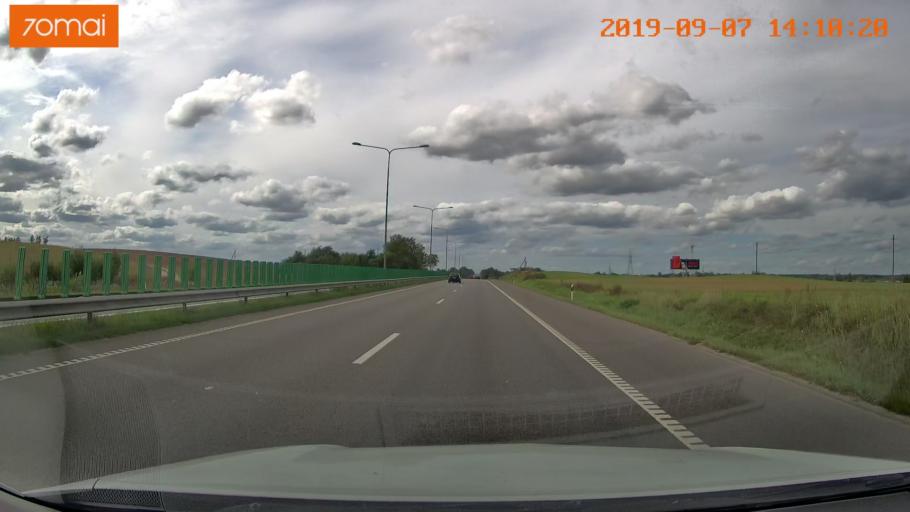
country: LT
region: Vilnius County
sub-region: Vilniaus Rajonas
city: Vievis
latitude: 54.7804
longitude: 24.7800
